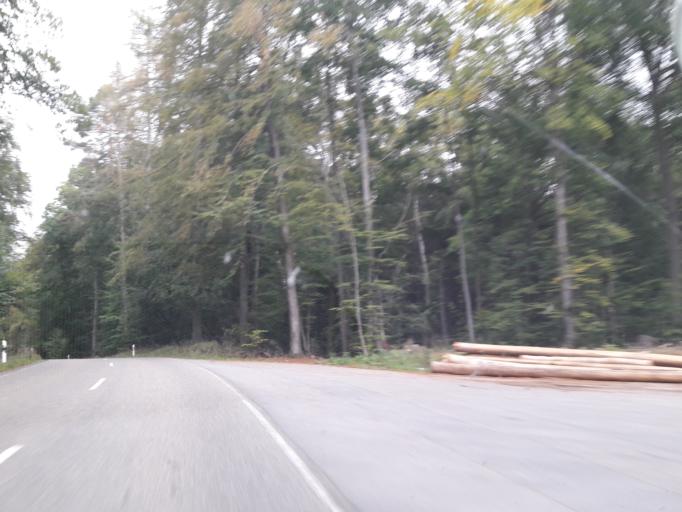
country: DE
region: Baden-Wuerttemberg
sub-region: Regierungsbezirk Stuttgart
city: Widdern
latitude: 49.2996
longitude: 9.3940
